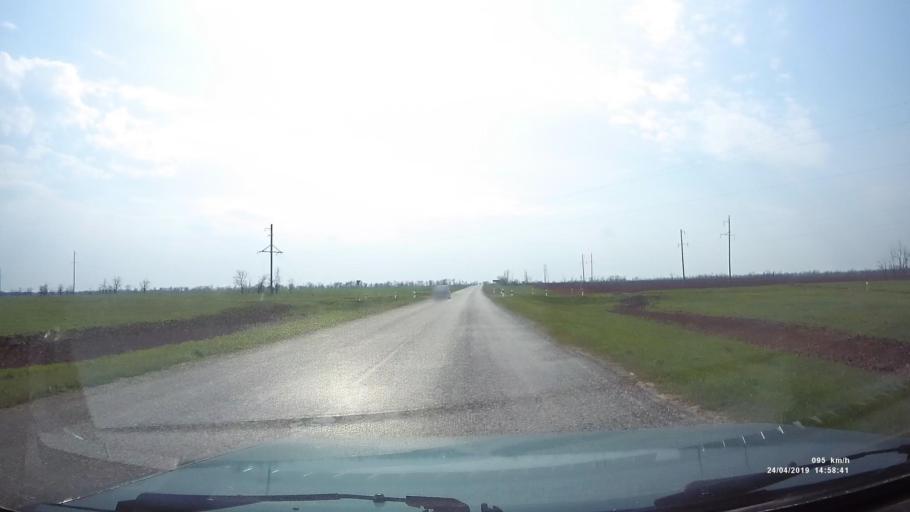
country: RU
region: Rostov
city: Remontnoye
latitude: 46.5681
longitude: 43.5928
